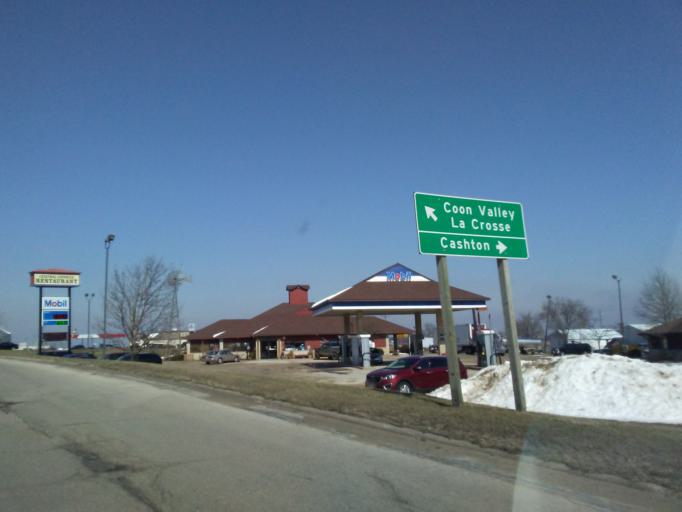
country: US
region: Wisconsin
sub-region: Vernon County
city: Westby
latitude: 43.6583
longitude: -90.8561
